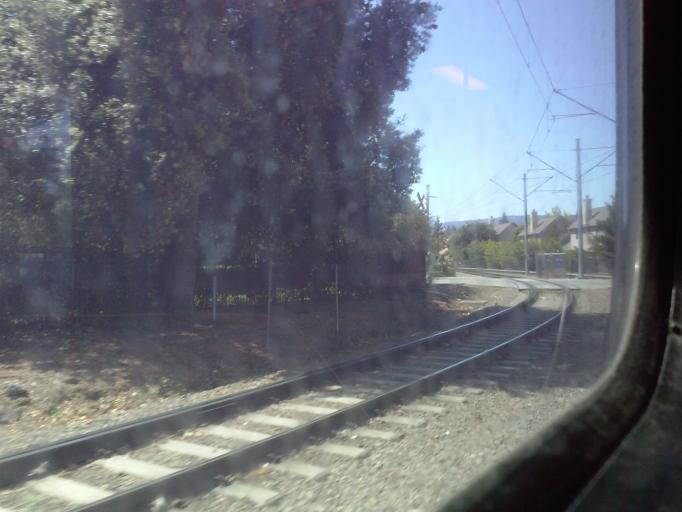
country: US
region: California
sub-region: Santa Clara County
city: Mountain View
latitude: 37.3915
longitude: -122.0596
